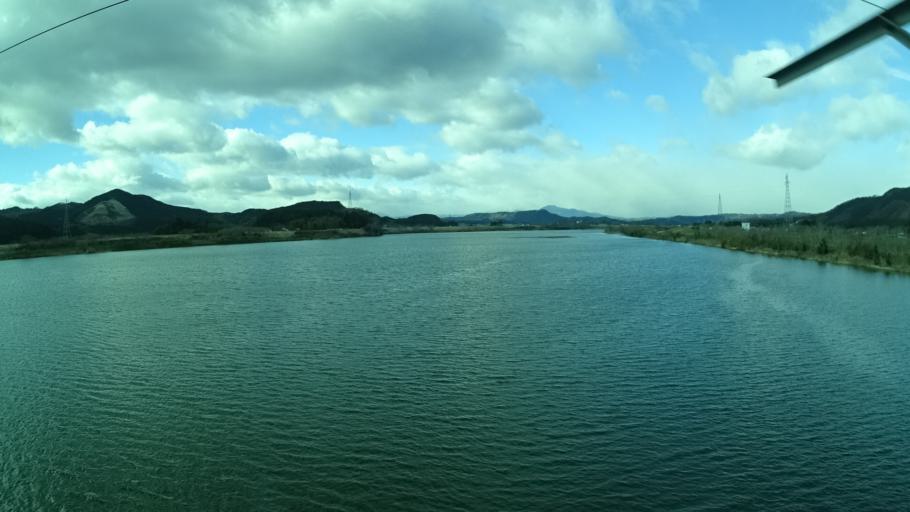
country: JP
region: Miyagi
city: Iwanuma
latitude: 38.0807
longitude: 140.8529
